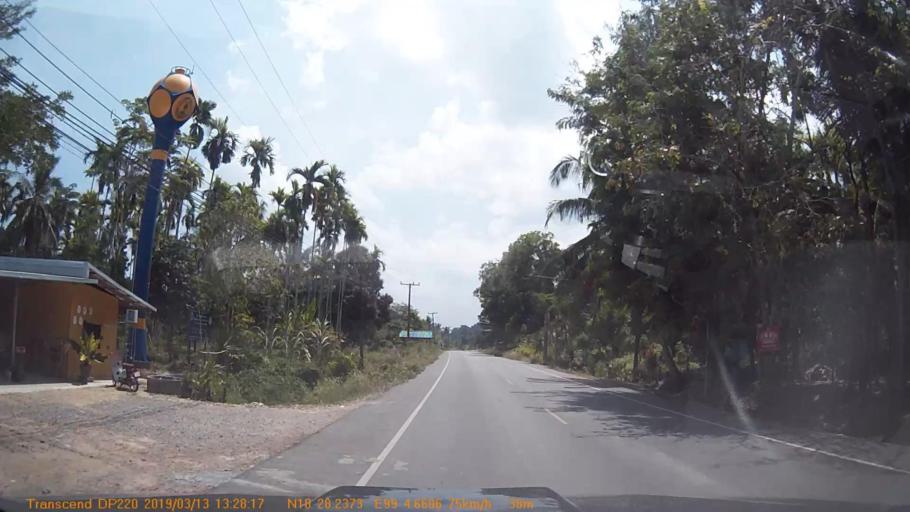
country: TH
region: Chumphon
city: Chumphon
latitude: 10.4751
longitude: 99.0780
